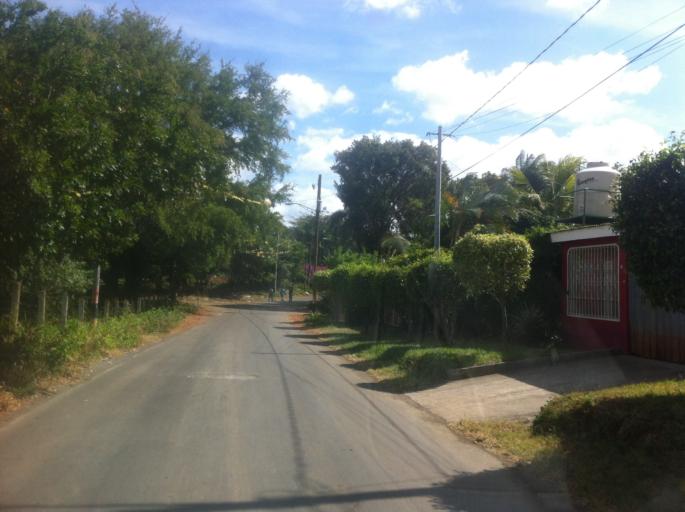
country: NI
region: Managua
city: Ciudad Sandino
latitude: 12.0755
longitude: -86.3276
